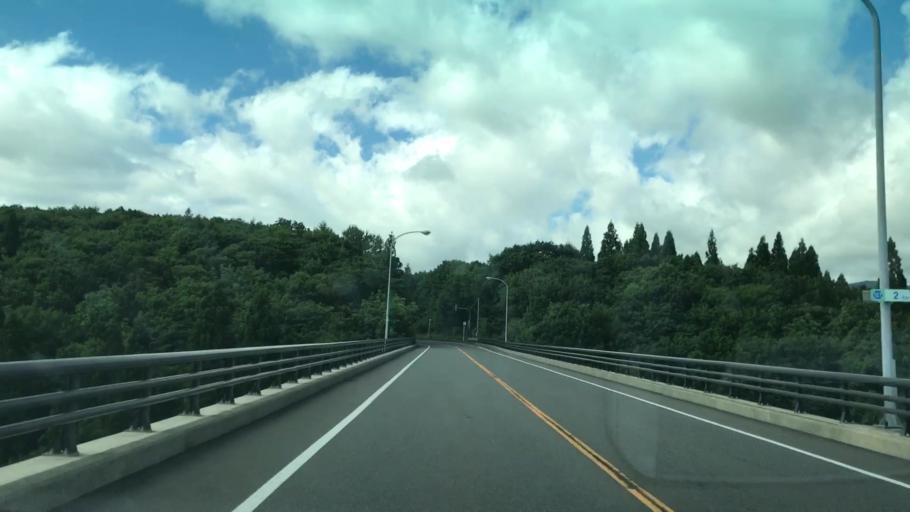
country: JP
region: Hokkaido
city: Muroran
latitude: 42.3789
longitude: 140.9656
